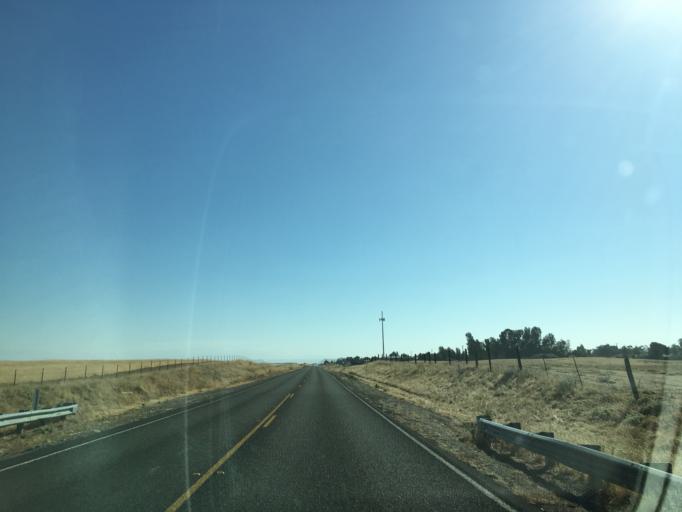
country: US
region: California
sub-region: Madera County
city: Bonadelle Ranchos-Madera Ranchos
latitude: 37.0103
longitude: -119.8983
